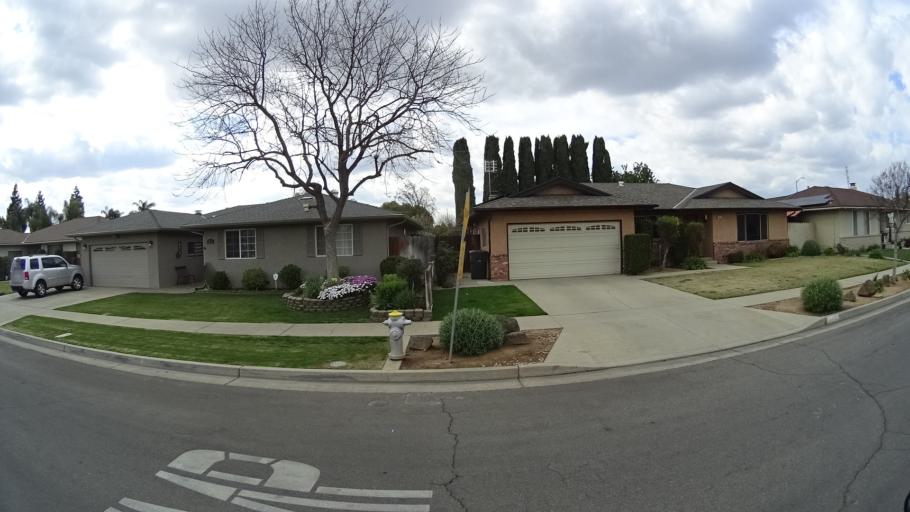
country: US
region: California
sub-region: Fresno County
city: Clovis
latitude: 36.8328
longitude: -119.7763
